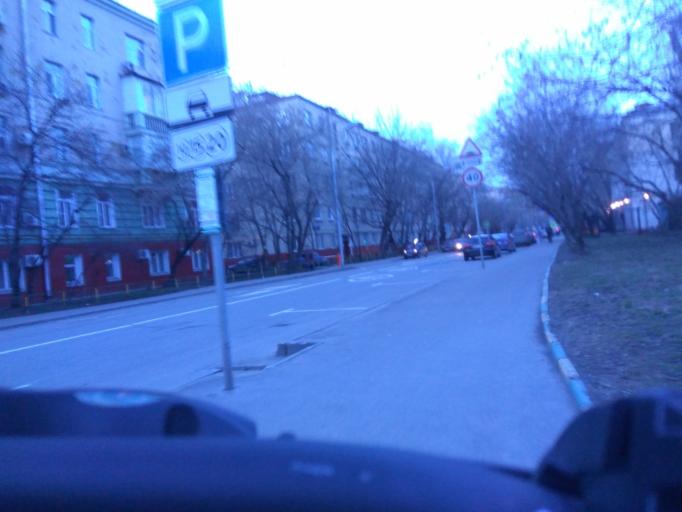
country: RU
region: Moskovskaya
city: Presnenskiy
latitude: 55.7405
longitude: 37.5443
